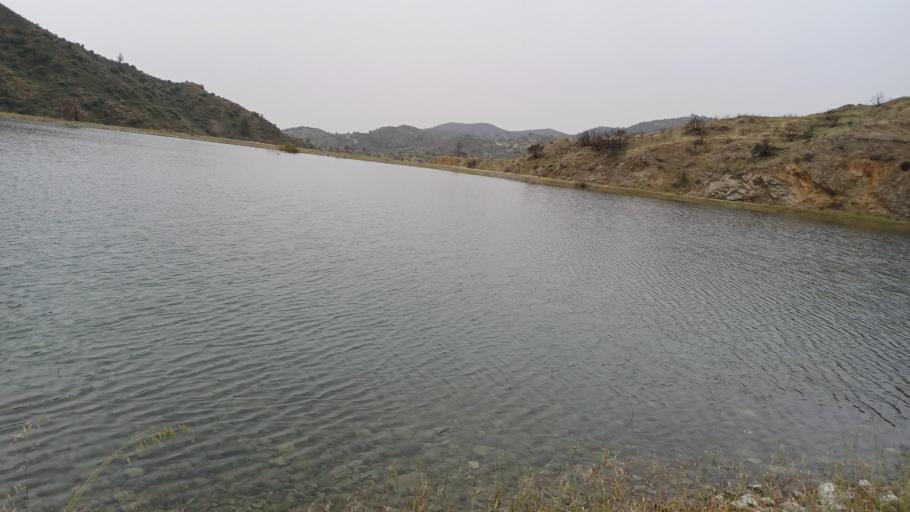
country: CY
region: Limassol
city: Parekklisha
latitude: 34.8400
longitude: 33.1211
